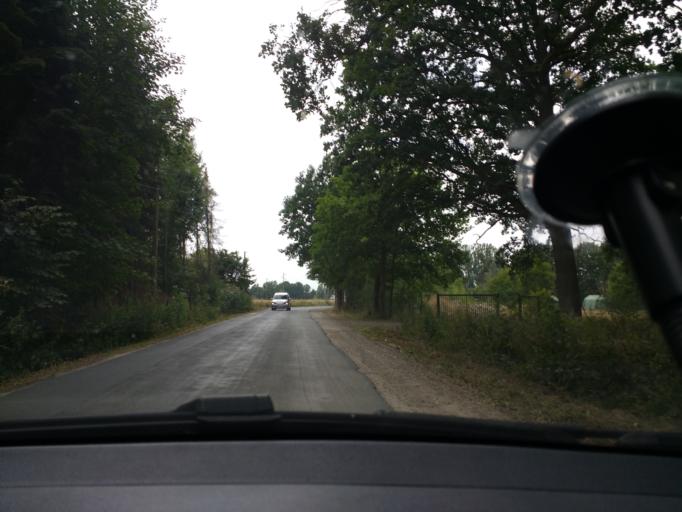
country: DE
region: Lower Saxony
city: Wagenhoff
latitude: 52.5177
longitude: 10.5520
